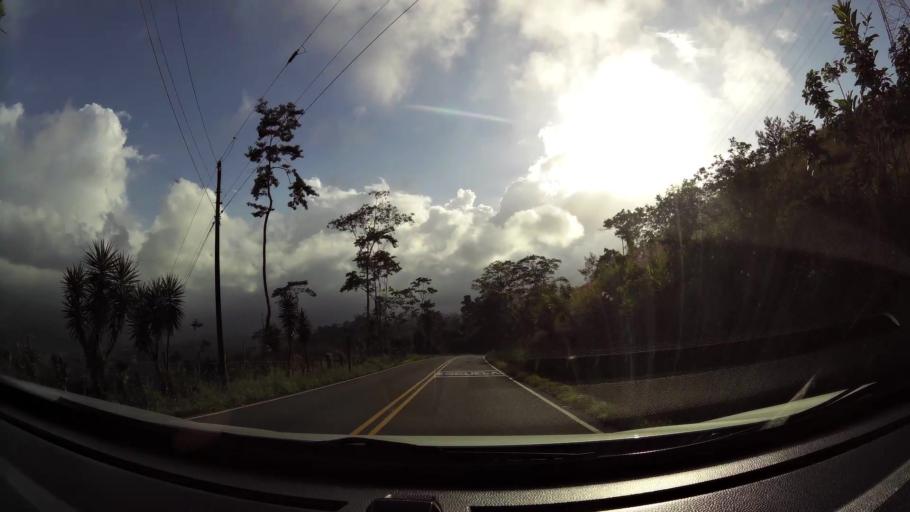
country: CR
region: Limon
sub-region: Canton de Siquirres
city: Siquirres
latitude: 10.0377
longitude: -83.5473
